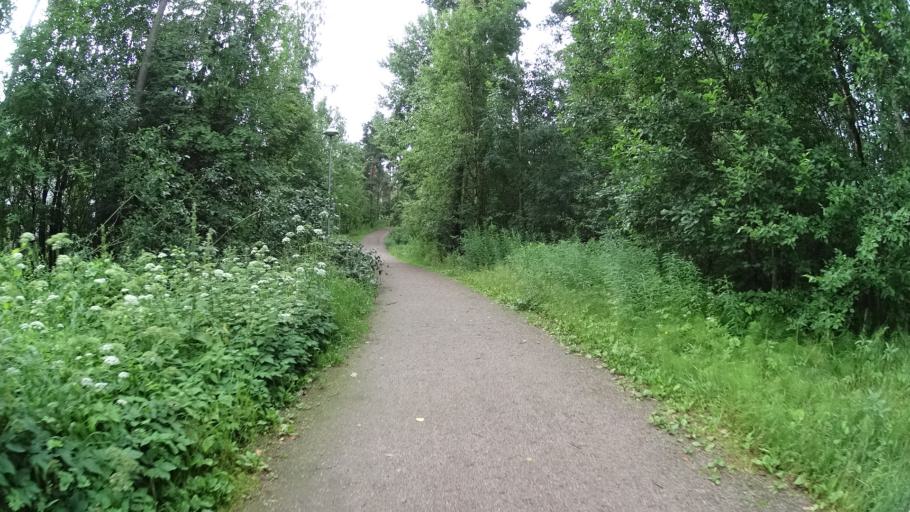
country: FI
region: Uusimaa
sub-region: Helsinki
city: Kilo
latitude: 60.2304
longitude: 24.8112
